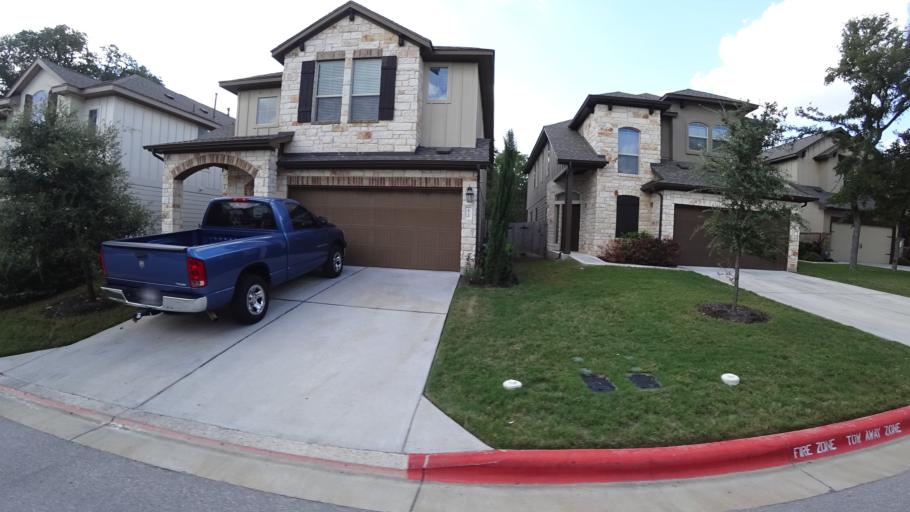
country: US
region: Texas
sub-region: Travis County
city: Manchaca
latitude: 30.1940
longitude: -97.8092
